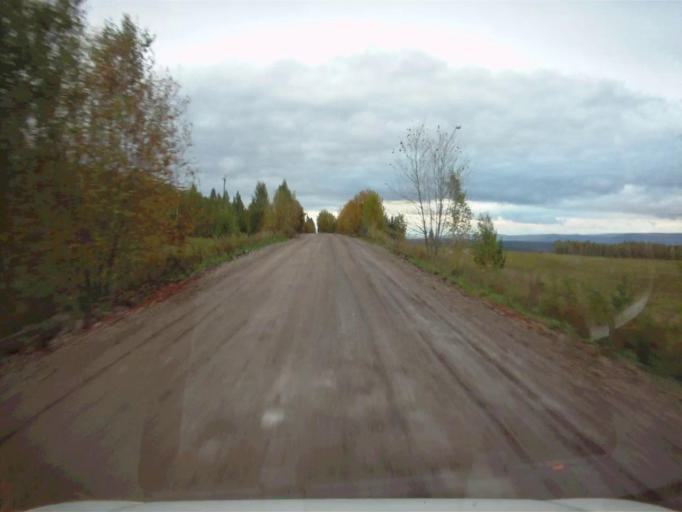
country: RU
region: Sverdlovsk
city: Mikhaylovsk
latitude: 56.1992
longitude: 59.2000
